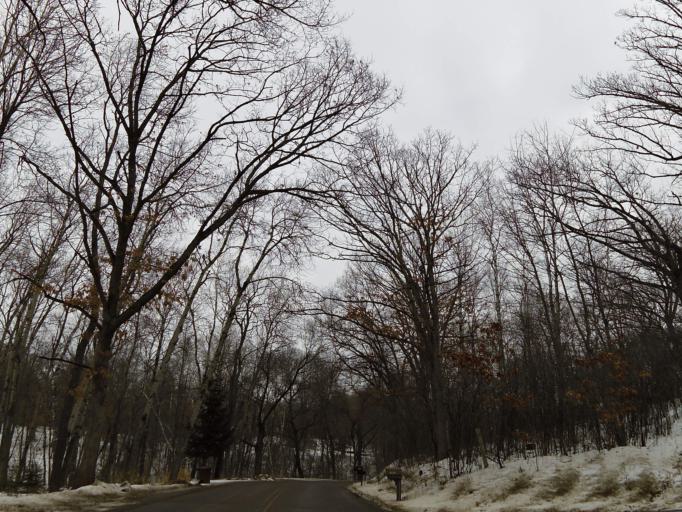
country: US
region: Minnesota
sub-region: Washington County
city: Bayport
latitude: 44.9944
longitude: -92.8023
